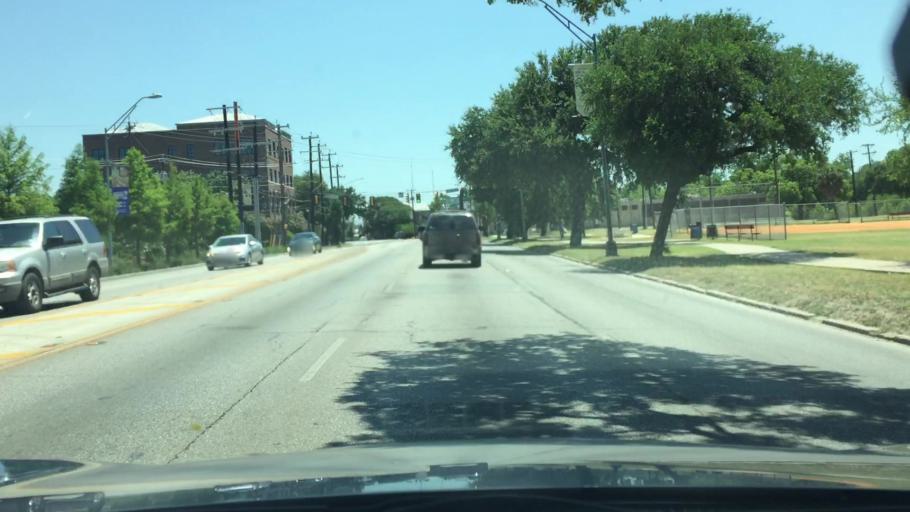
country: US
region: Texas
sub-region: Bexar County
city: Olmos Park
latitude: 29.4527
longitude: -98.4728
